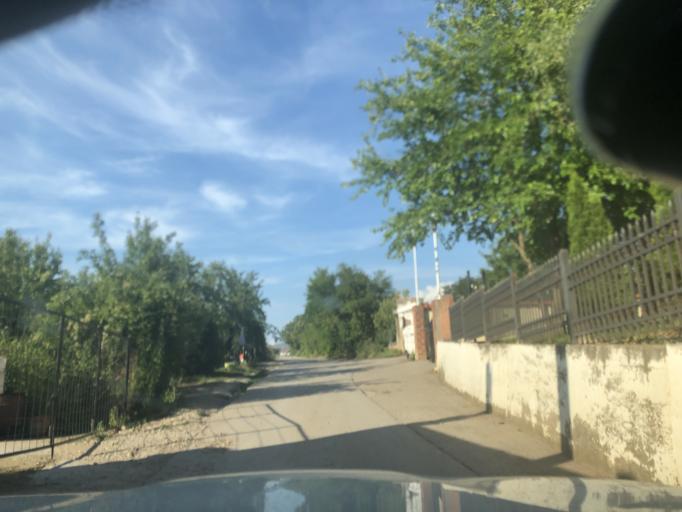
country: RS
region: Central Serbia
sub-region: Nisavski Okrug
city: Nis
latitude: 43.3228
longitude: 21.9519
